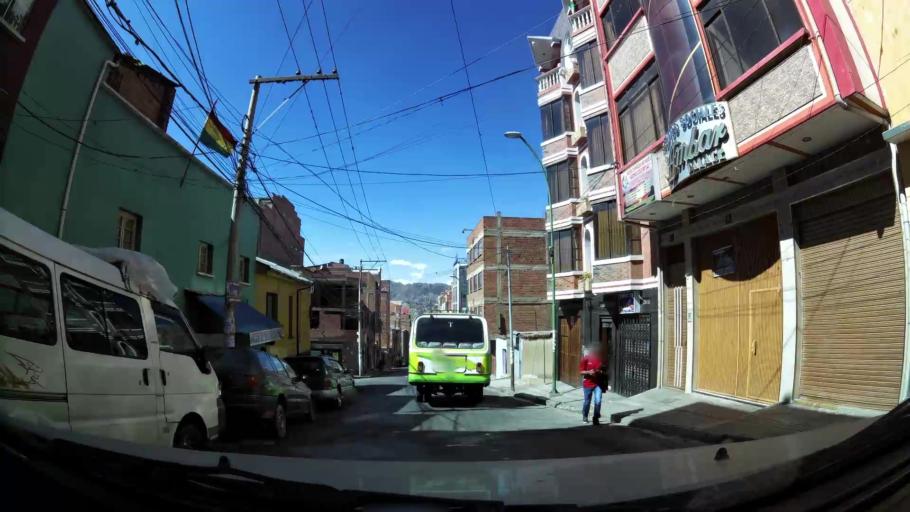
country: BO
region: La Paz
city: La Paz
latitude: -16.4972
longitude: -68.1486
